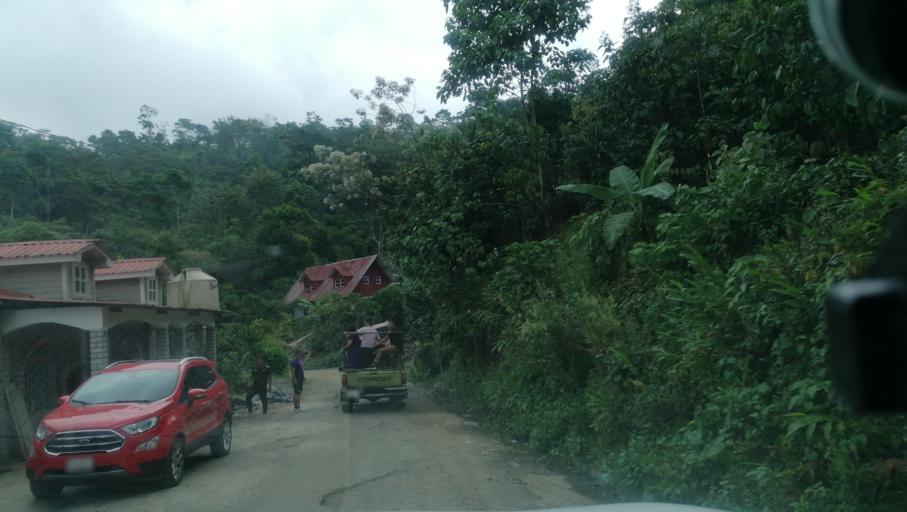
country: MX
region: Chiapas
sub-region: Cacahoatan
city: Benito Juarez
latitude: 15.0726
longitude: -92.1683
